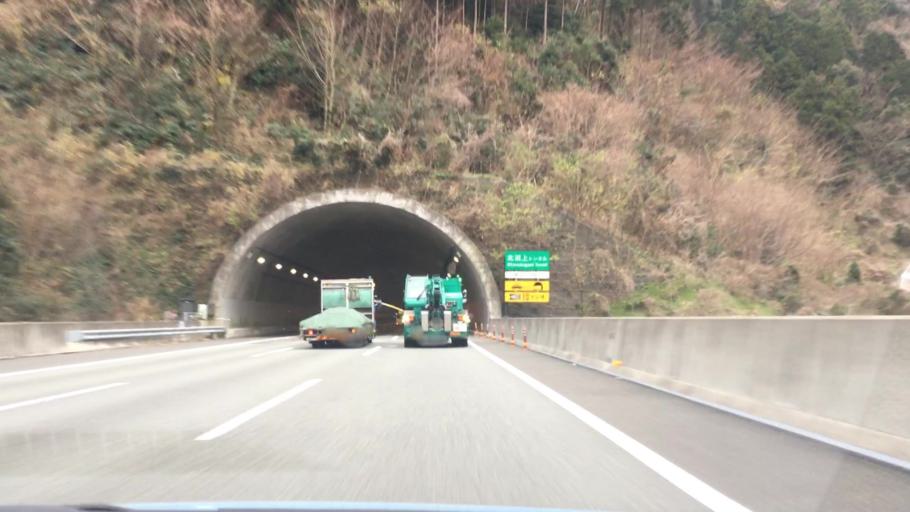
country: JP
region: Shizuoka
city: Shizuoka-shi
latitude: 35.0541
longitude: 138.4228
